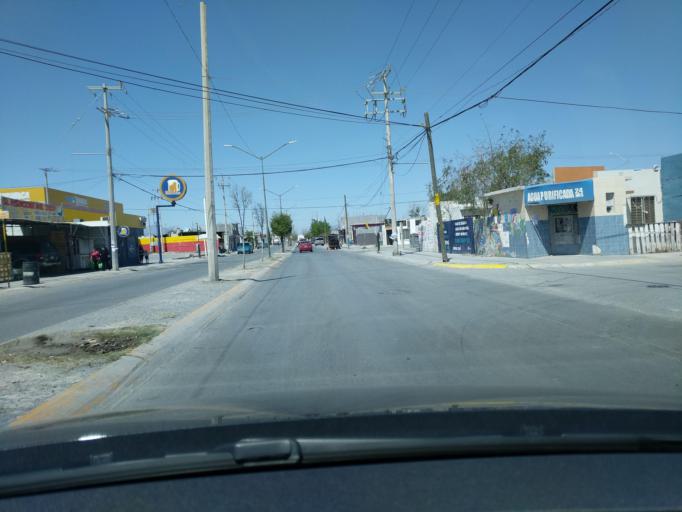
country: MX
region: Nuevo Leon
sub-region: Pesqueria
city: Colinas del Aeropuerto
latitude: 25.8223
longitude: -100.1094
